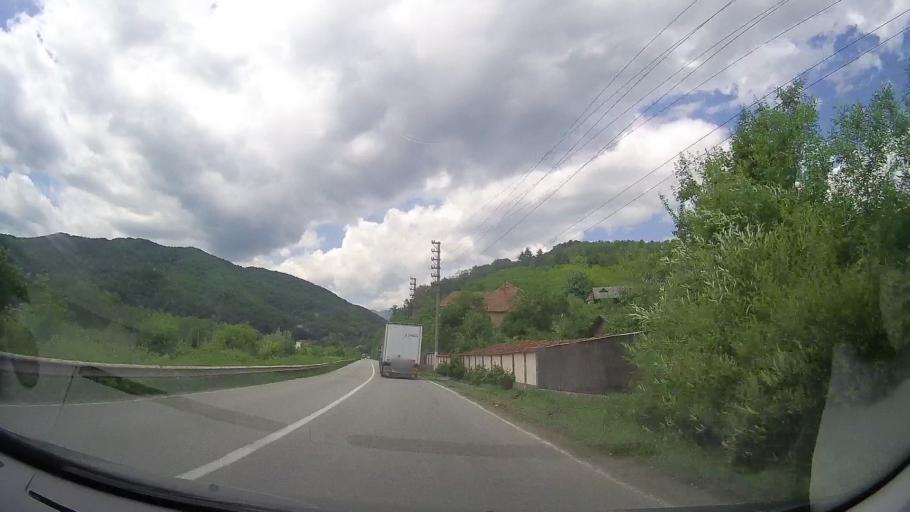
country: RO
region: Valcea
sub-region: Oras Calimanesti
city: Jiblea Veche
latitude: 45.2462
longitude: 24.3467
